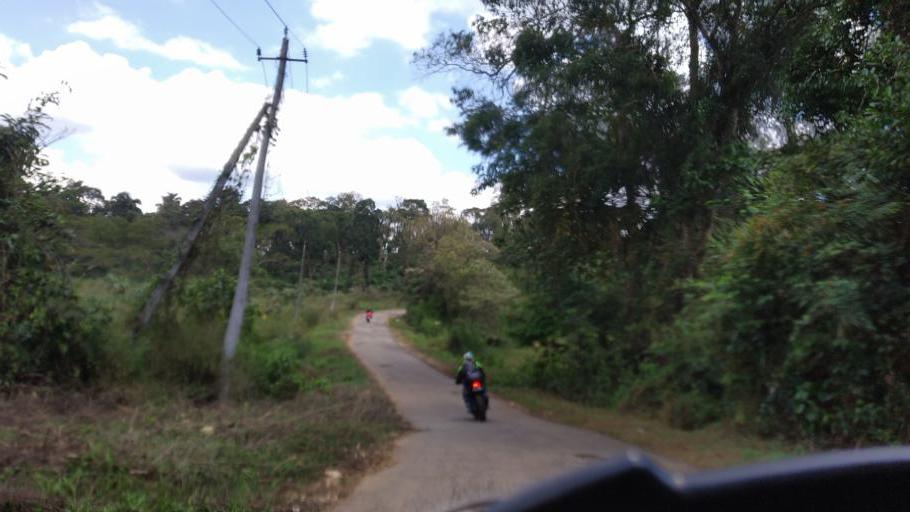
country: IN
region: Karnataka
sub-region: Kodagu
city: Ponnampet
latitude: 12.0241
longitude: 75.8908
